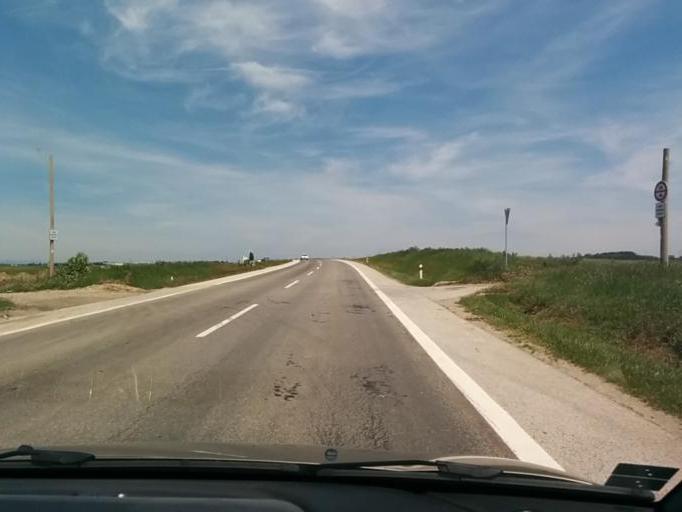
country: SK
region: Trnavsky
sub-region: Okres Galanta
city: Galanta
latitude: 48.2546
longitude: 17.7101
